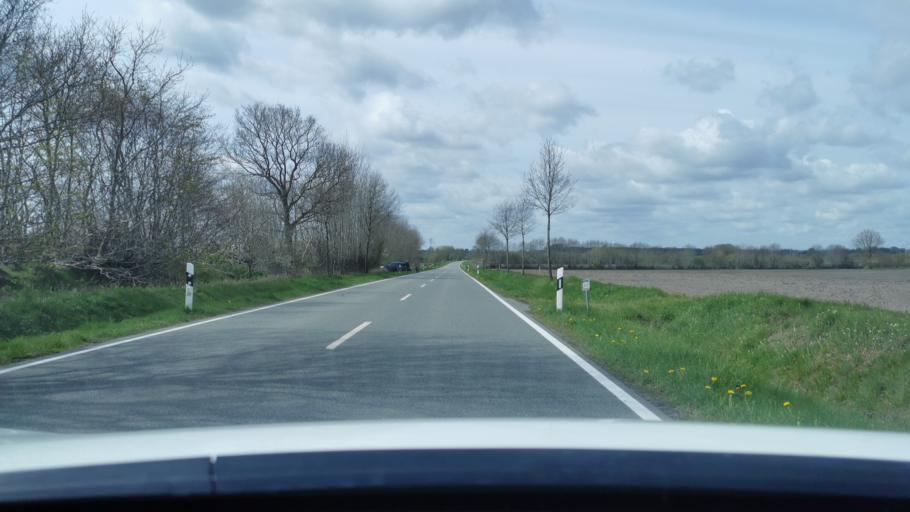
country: DE
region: Schleswig-Holstein
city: Breiholz
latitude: 54.1989
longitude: 9.5113
